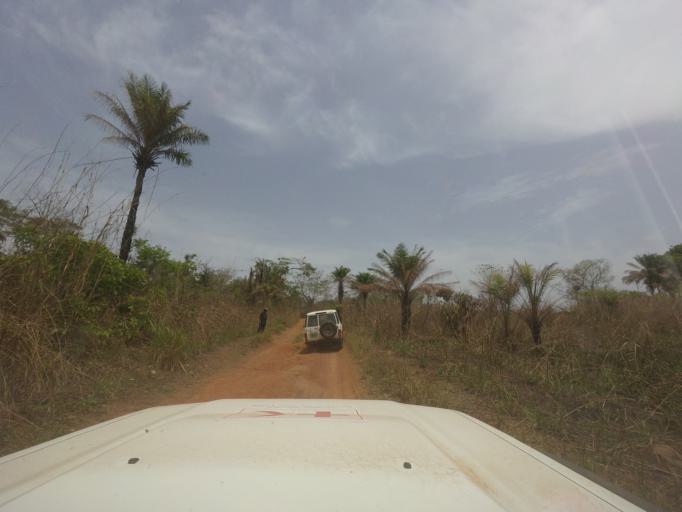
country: SL
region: Eastern Province
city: Buedu
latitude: 8.4708
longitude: -10.3334
